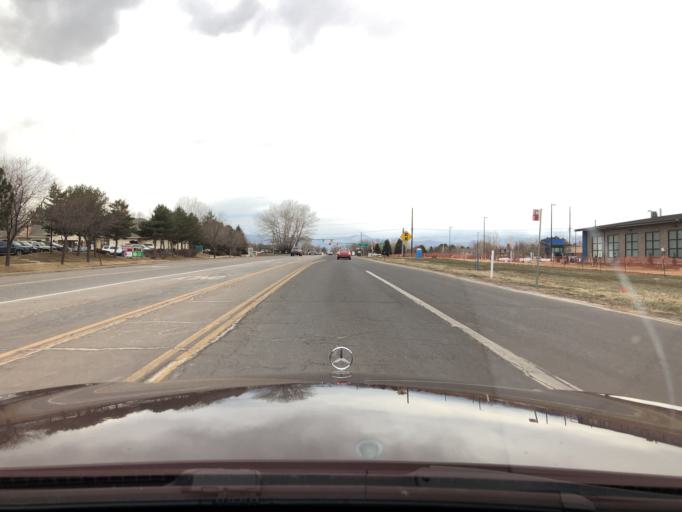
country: US
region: Colorado
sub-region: Boulder County
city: Louisville
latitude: 40.0147
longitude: -105.1280
